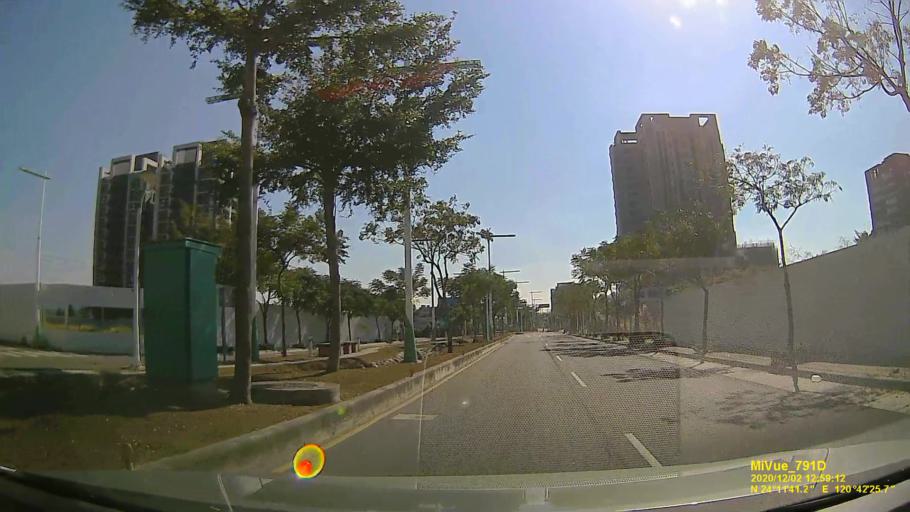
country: TW
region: Taiwan
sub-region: Taichung City
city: Taichung
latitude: 24.1948
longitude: 120.7071
